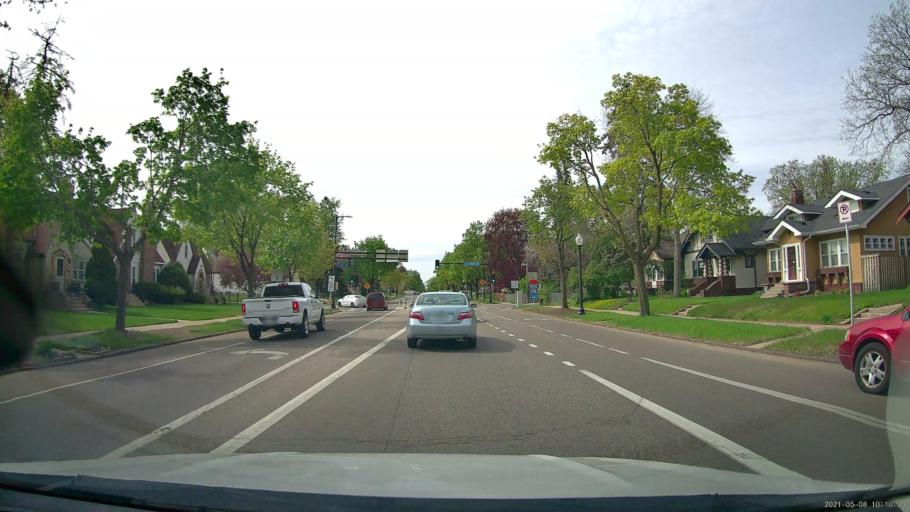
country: US
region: Minnesota
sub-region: Hennepin County
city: Richfield
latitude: 44.9203
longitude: -93.2677
